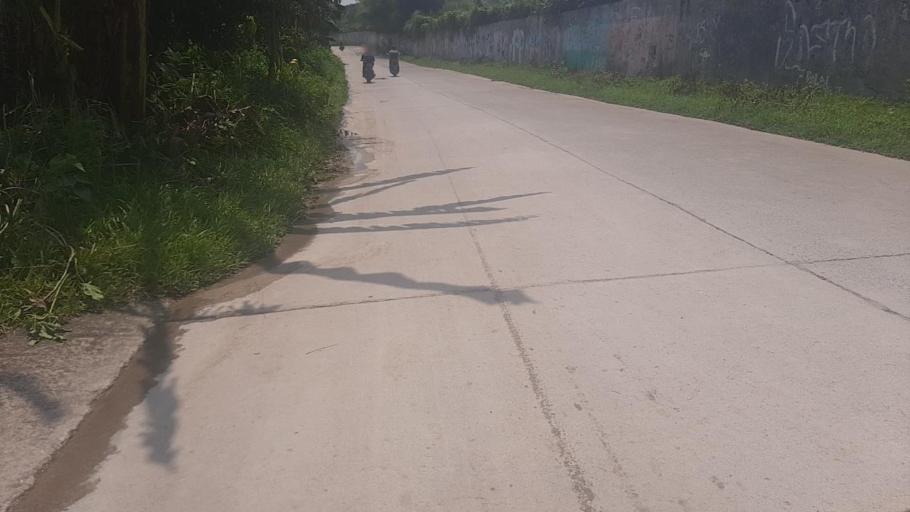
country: ID
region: West Java
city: Citeureup
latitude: -6.4646
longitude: 106.9306
